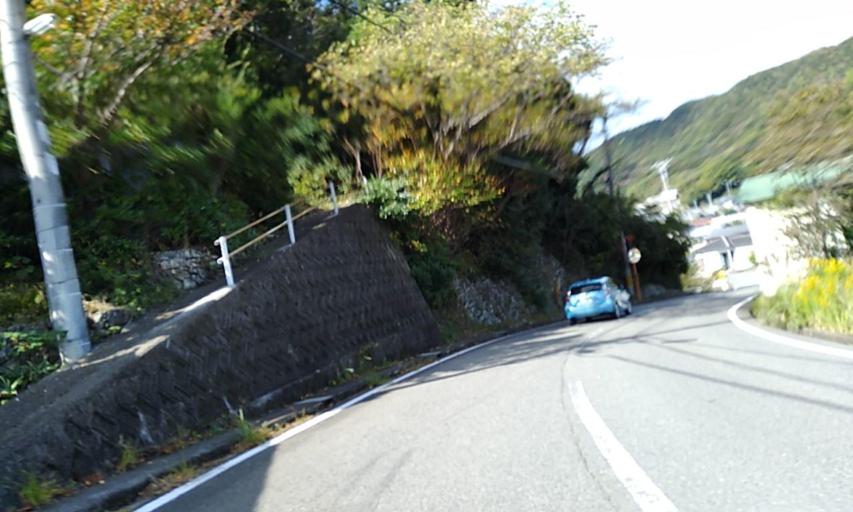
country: JP
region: Wakayama
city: Gobo
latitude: 33.9677
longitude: 135.0894
